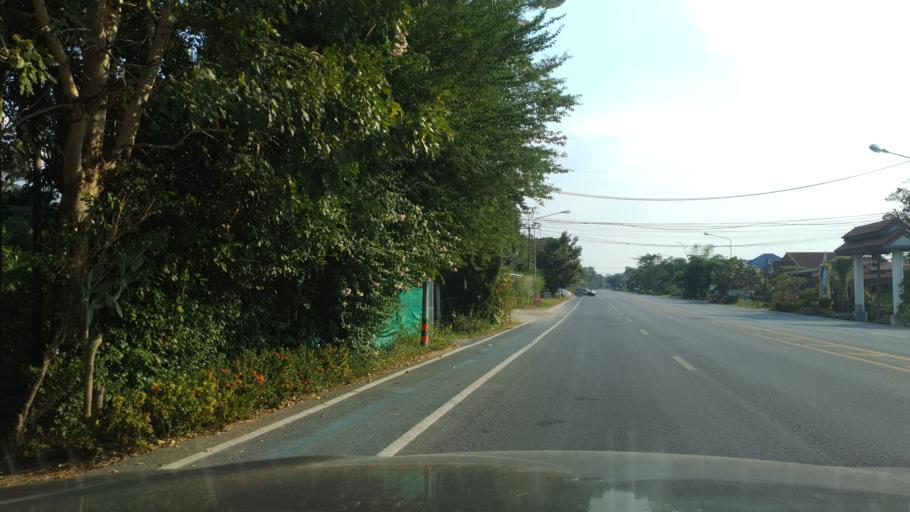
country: TH
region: Tak
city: Tak
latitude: 16.8649
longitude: 99.1202
